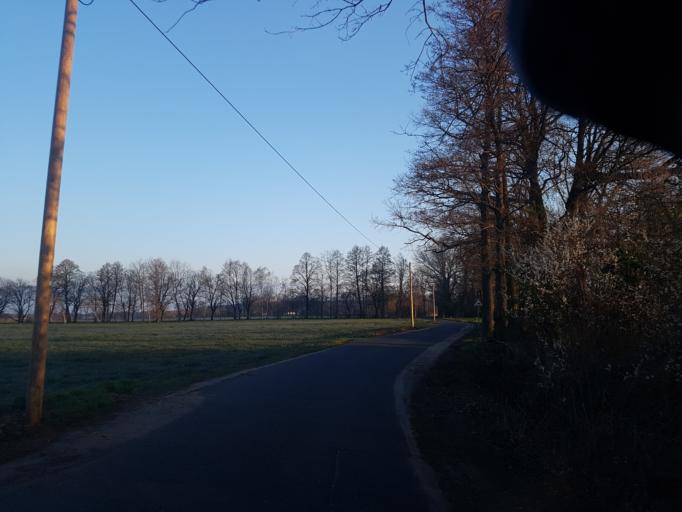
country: DE
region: Brandenburg
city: Schilda
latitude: 51.6302
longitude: 13.3105
